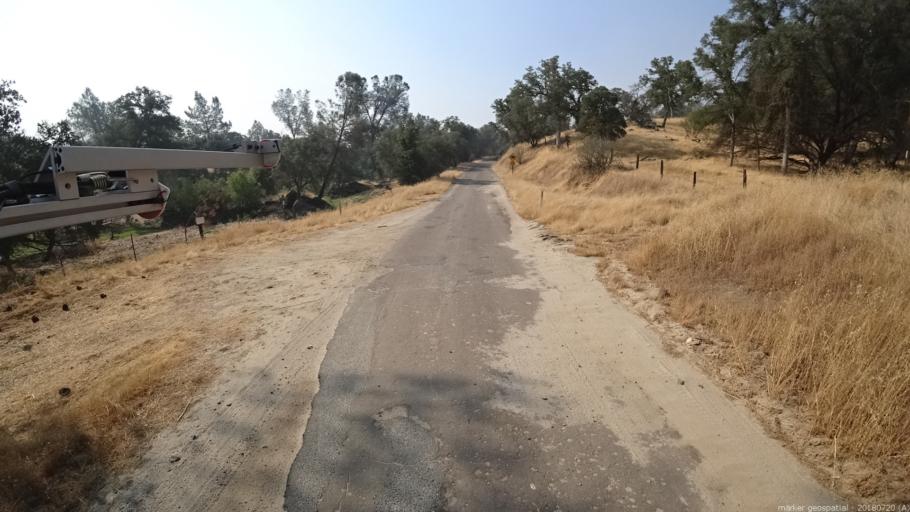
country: US
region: California
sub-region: Madera County
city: Ahwahnee
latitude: 37.3248
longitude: -119.8791
